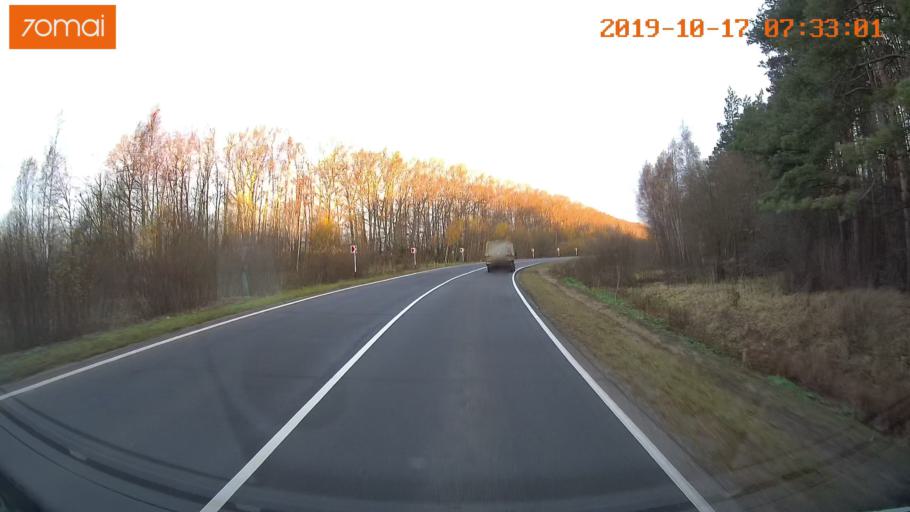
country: RU
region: Ivanovo
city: Gavrilov Posad
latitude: 56.4015
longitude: 39.9628
